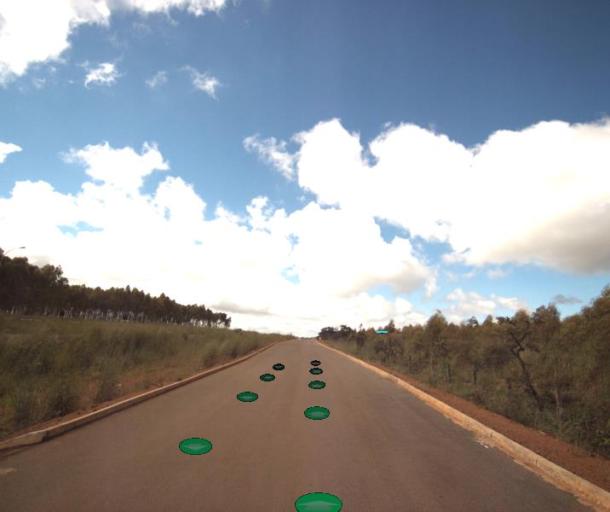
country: BR
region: Goias
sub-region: Anapolis
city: Anapolis
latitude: -16.2346
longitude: -49.0073
